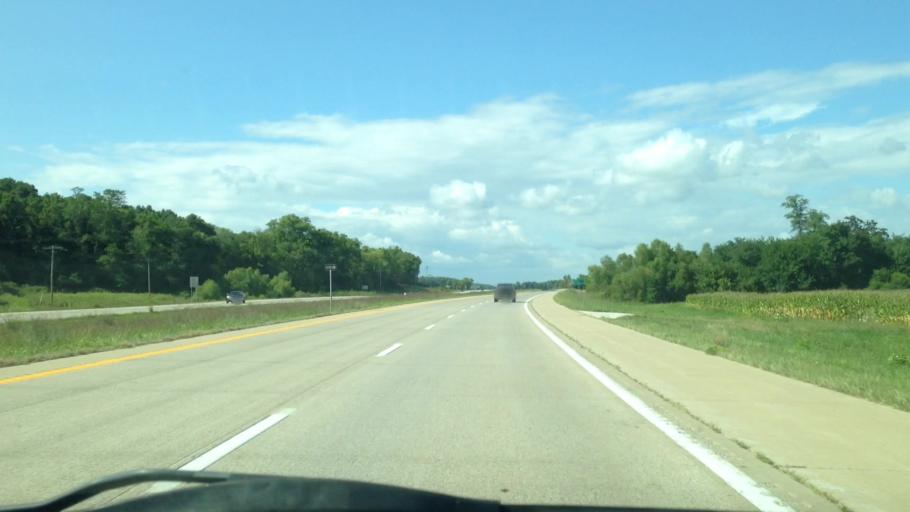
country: US
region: Illinois
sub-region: Hancock County
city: Warsaw
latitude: 40.2814
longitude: -91.5649
